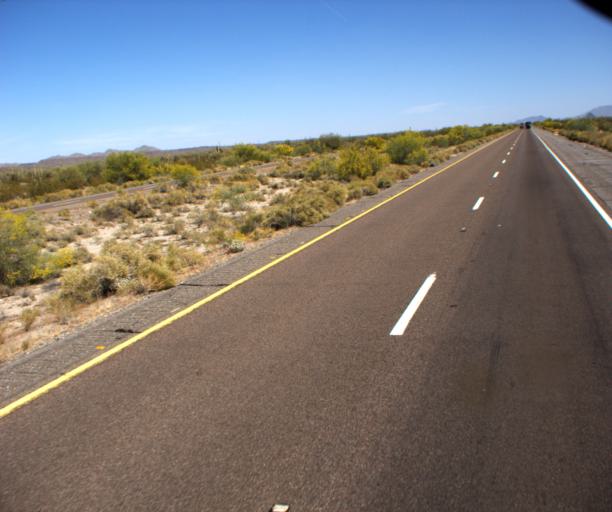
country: US
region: Arizona
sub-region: Maricopa County
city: Gila Bend
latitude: 32.8593
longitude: -112.3913
